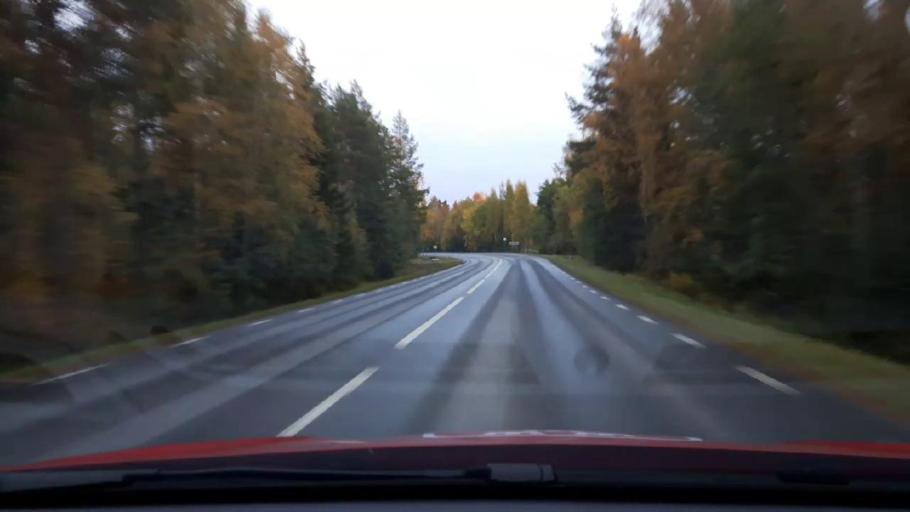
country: SE
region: Jaemtland
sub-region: OEstersunds Kommun
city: Ostersund
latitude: 63.2121
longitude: 14.6259
